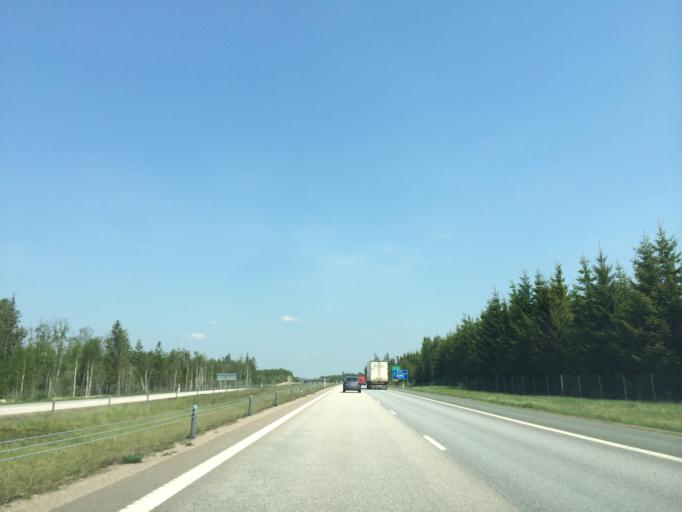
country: SE
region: Kronoberg
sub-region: Ljungby Kommun
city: Lagan
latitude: 57.0280
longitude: 14.0470
